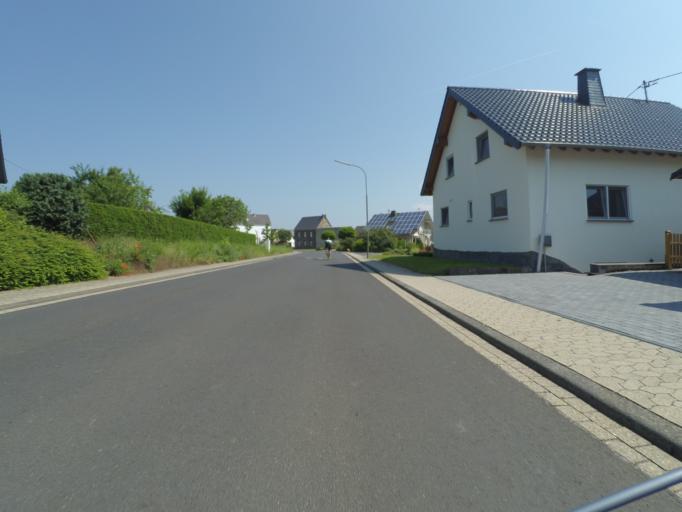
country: DE
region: Rheinland-Pfalz
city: Kehrig
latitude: 50.2943
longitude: 7.2280
